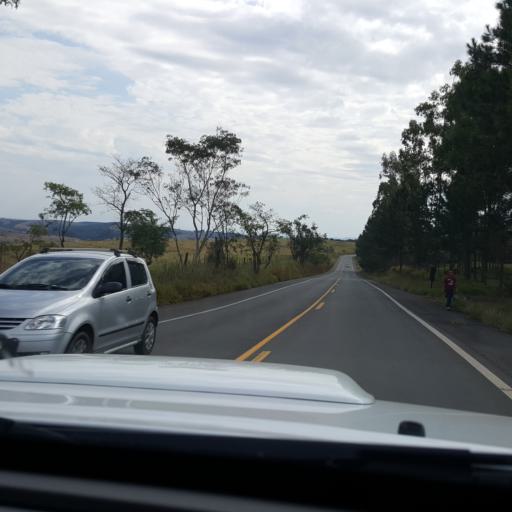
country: BR
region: Sao Paulo
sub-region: Itaporanga
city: Itaporanga
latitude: -23.7731
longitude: -49.4363
